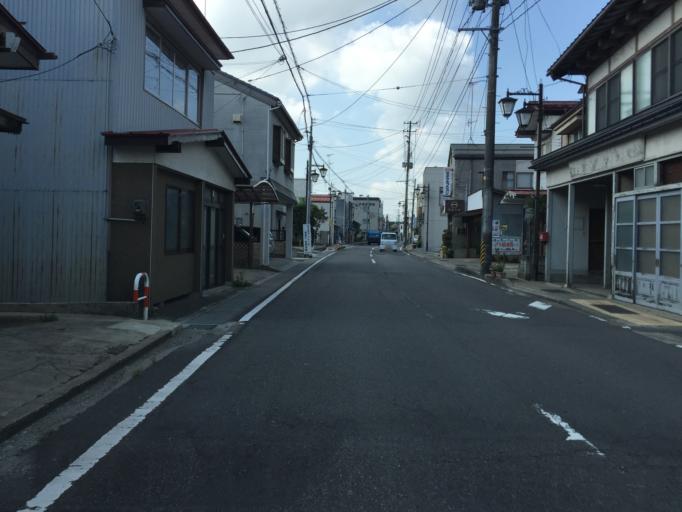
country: JP
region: Fukushima
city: Motomiya
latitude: 37.5207
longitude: 140.4062
